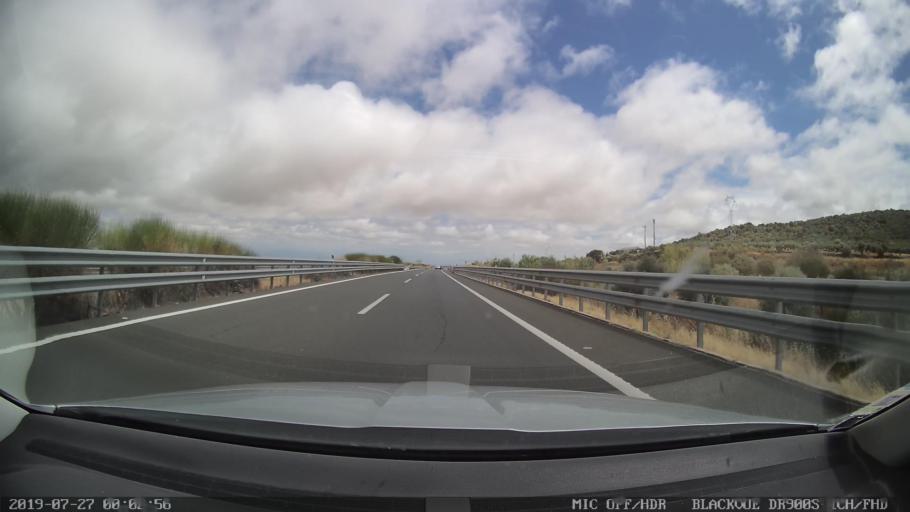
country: ES
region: Extremadura
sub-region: Provincia de Caceres
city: Almaraz
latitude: 39.8079
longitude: -5.6700
